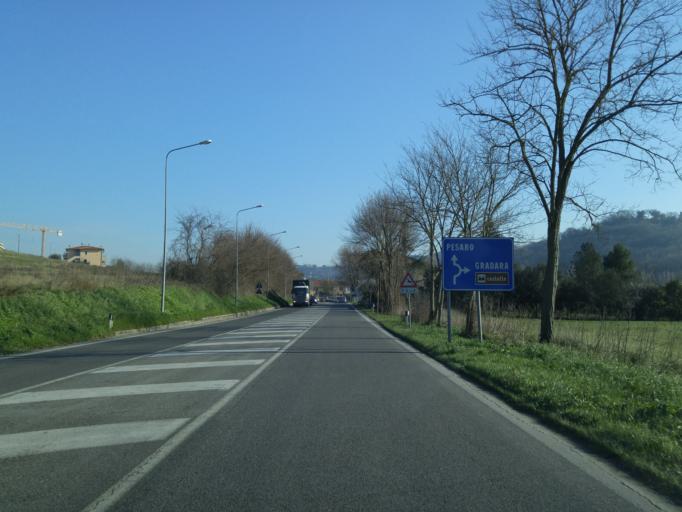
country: IT
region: The Marches
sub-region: Provincia di Pesaro e Urbino
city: Gradara
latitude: 43.9499
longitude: 12.7879
